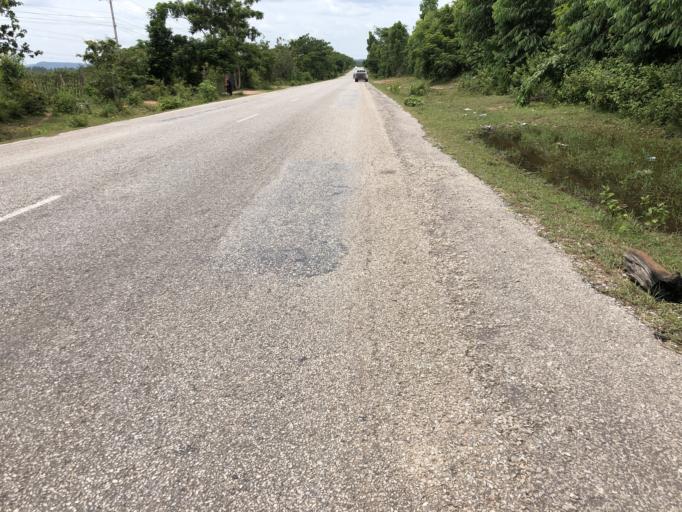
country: TH
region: Nakhon Phanom
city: That Phanom
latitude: 17.0408
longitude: 104.9953
